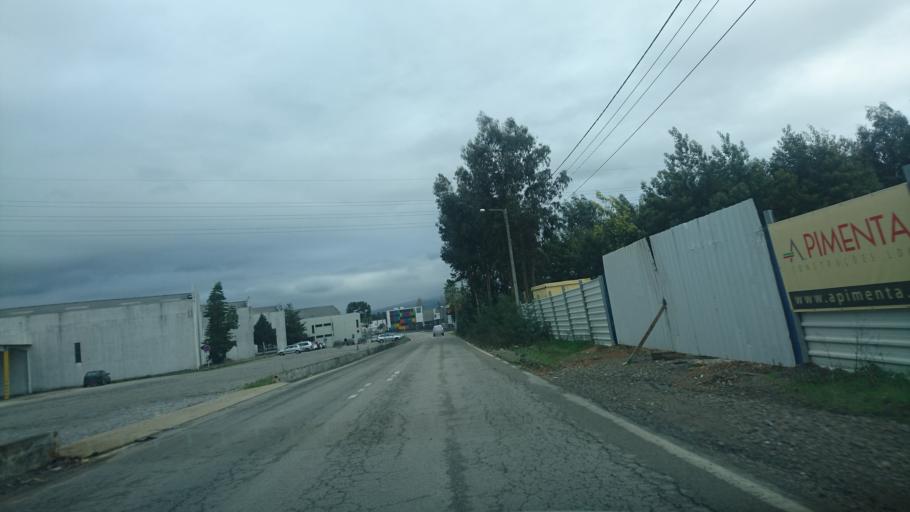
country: PT
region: Aveiro
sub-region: Agueda
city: Valongo
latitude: 40.5975
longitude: -8.4486
